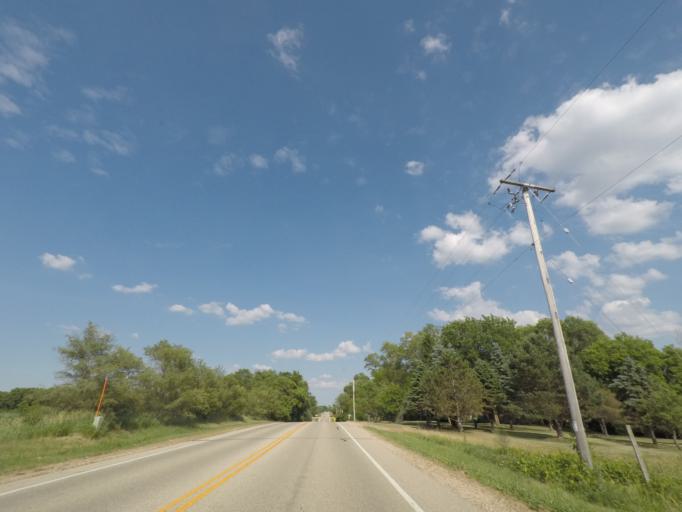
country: US
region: Wisconsin
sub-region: Waukesha County
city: Eagle
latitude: 42.7932
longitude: -88.5112
